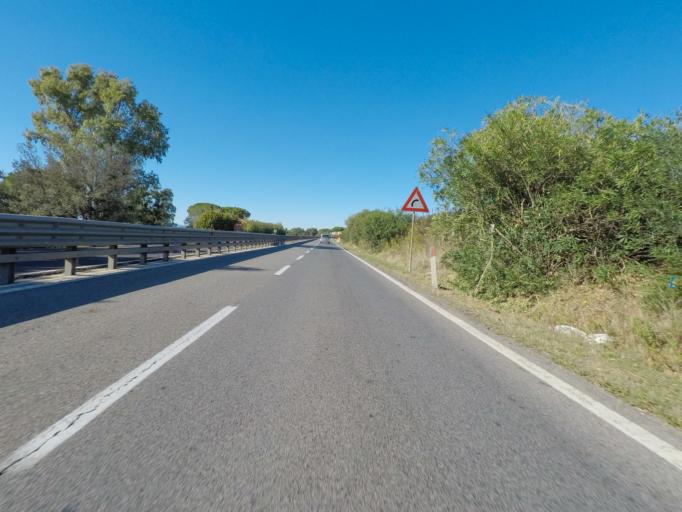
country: IT
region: Tuscany
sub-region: Provincia di Grosseto
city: Grosseto
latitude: 42.7200
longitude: 11.1400
